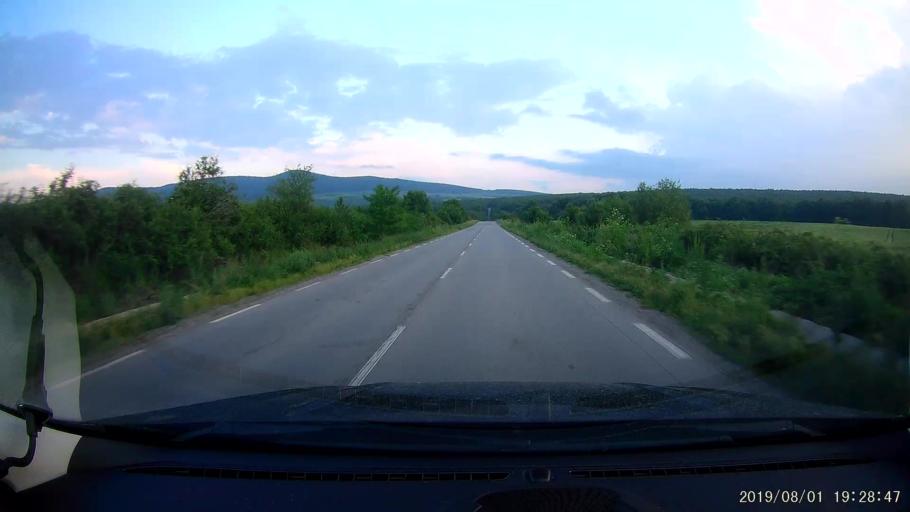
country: BG
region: Burgas
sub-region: Obshtina Sungurlare
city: Sungurlare
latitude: 42.8375
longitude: 26.9134
